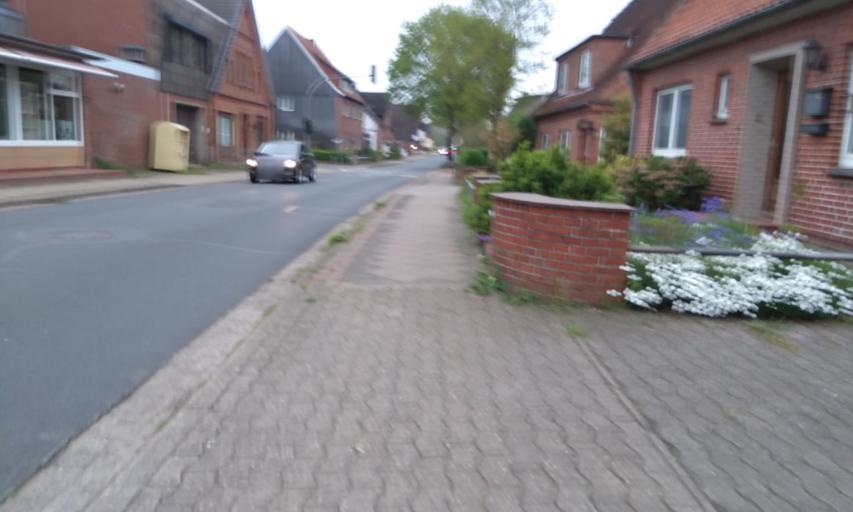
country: DE
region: Lower Saxony
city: Harsefeld
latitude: 53.4568
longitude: 9.5034
